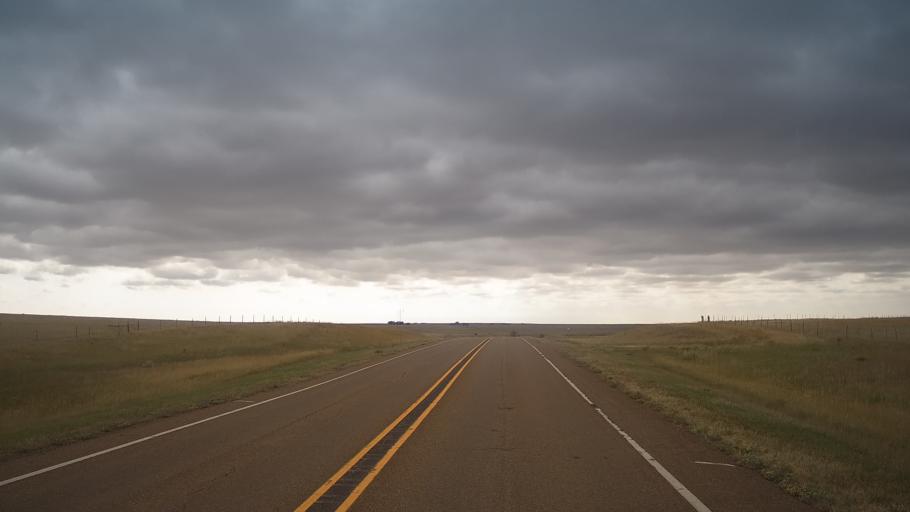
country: US
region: Montana
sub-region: Valley County
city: Glasgow
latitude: 48.3677
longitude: -106.7896
